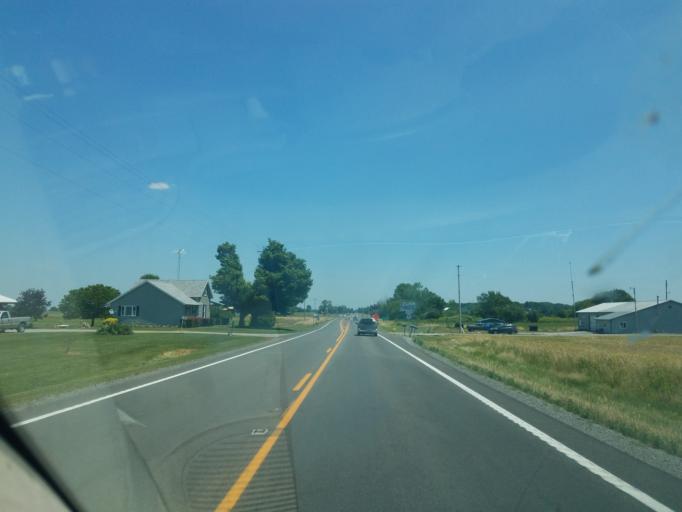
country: US
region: Ohio
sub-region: Hardin County
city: Ada
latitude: 40.7329
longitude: -83.8271
